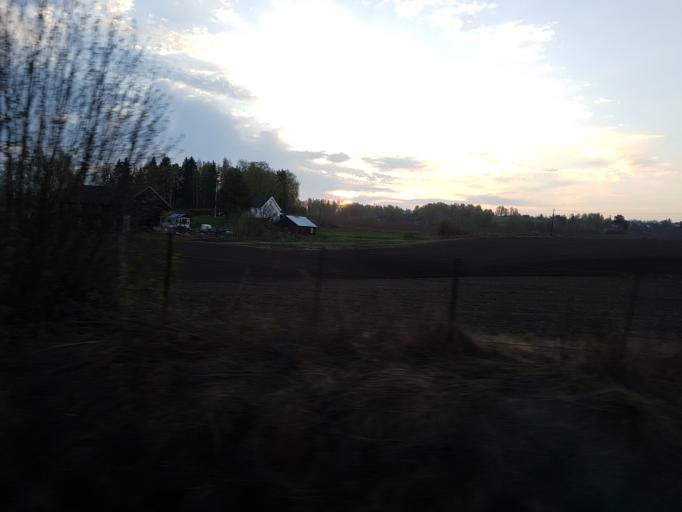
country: NO
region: Hedmark
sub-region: Hamar
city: Hamar
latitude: 60.7604
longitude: 11.1056
